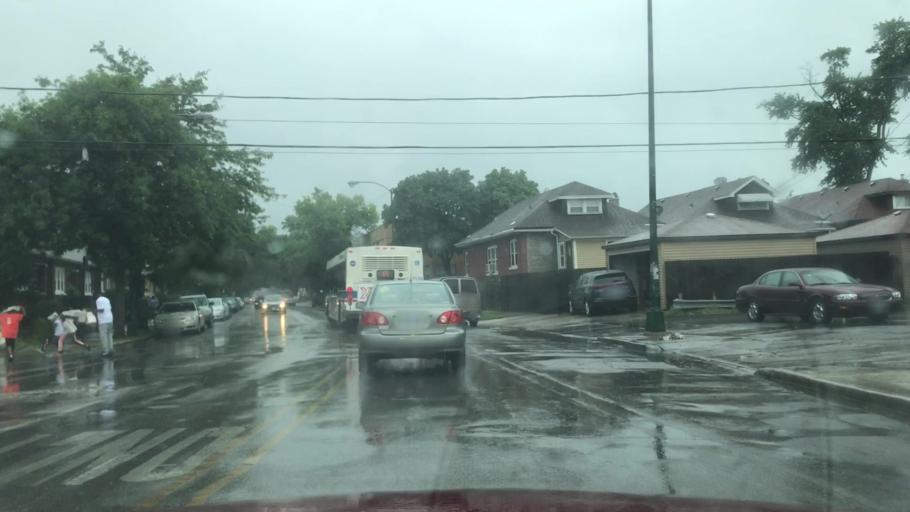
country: US
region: Illinois
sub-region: Cook County
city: Oak Park
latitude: 41.9097
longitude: -87.7557
